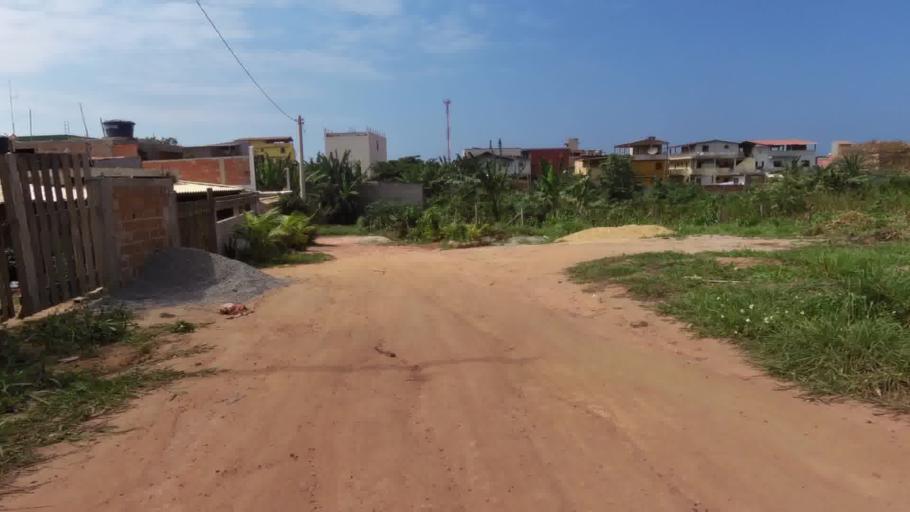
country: BR
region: Espirito Santo
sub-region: Marataizes
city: Marataizes
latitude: -21.0242
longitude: -40.8181
